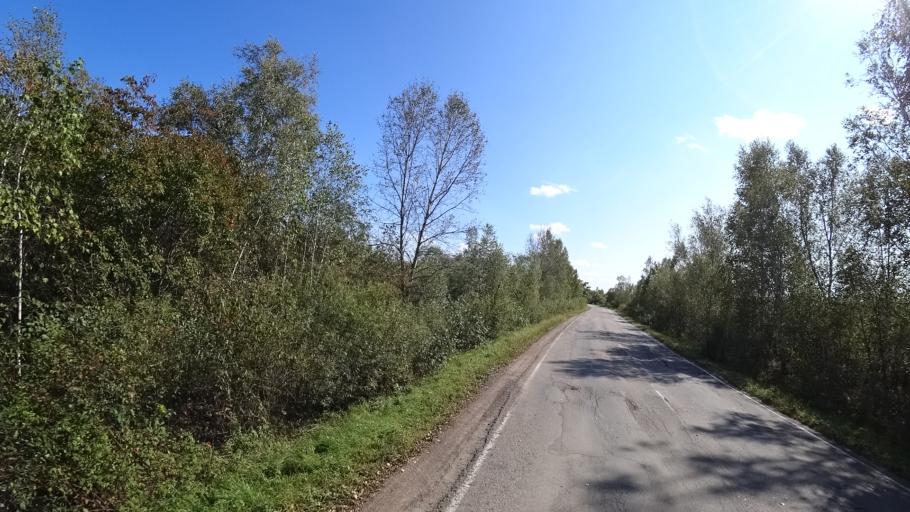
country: RU
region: Amur
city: Arkhara
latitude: 49.4038
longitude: 130.1284
